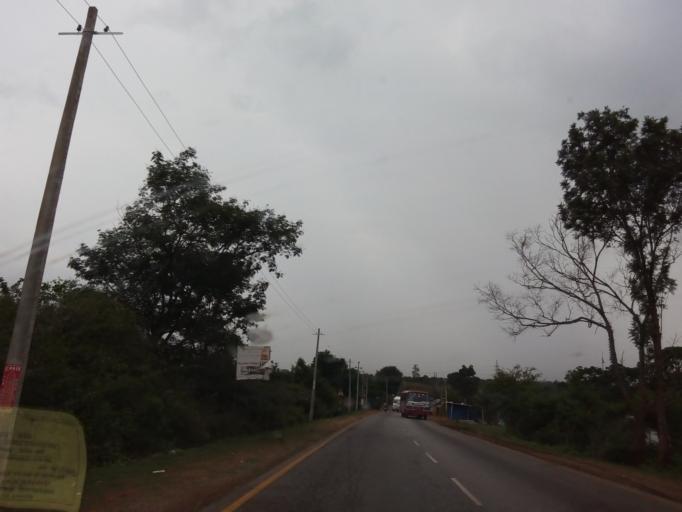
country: IN
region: Karnataka
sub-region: Hassan
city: Hassan
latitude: 13.0926
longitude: 76.0289
